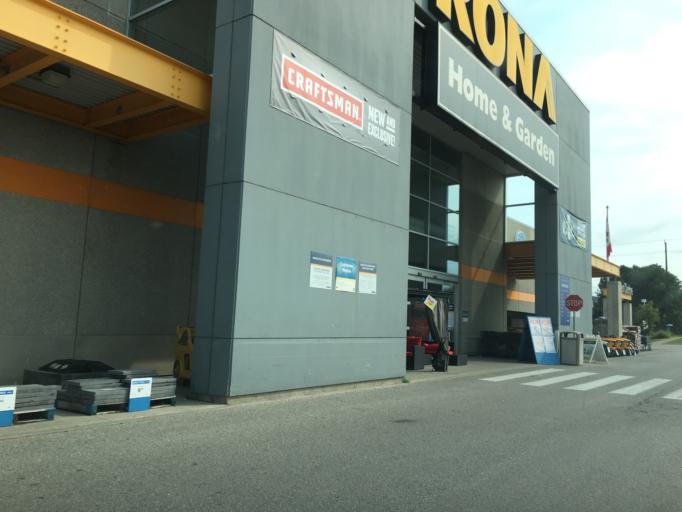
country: CA
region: Ontario
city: Markham
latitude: 43.8165
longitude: -79.2947
